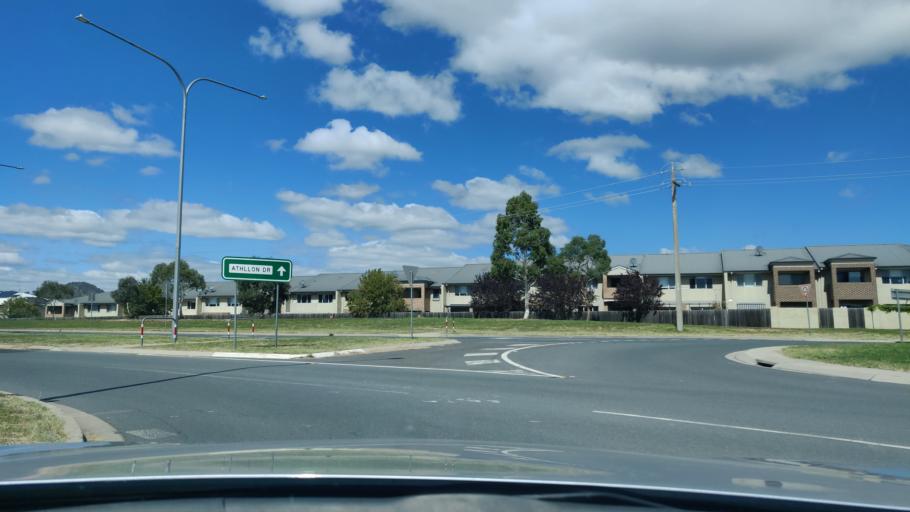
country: AU
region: Australian Capital Territory
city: Macarthur
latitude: -35.4248
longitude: 149.0703
